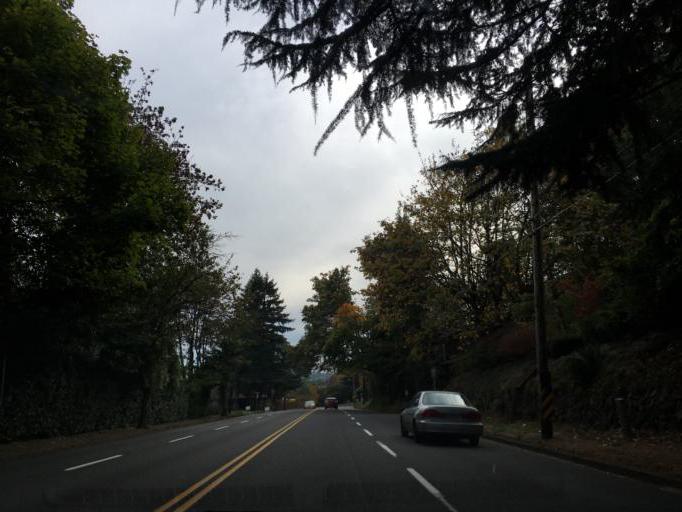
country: US
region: Oregon
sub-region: Multnomah County
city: Lents
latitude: 45.5202
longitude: -122.5879
